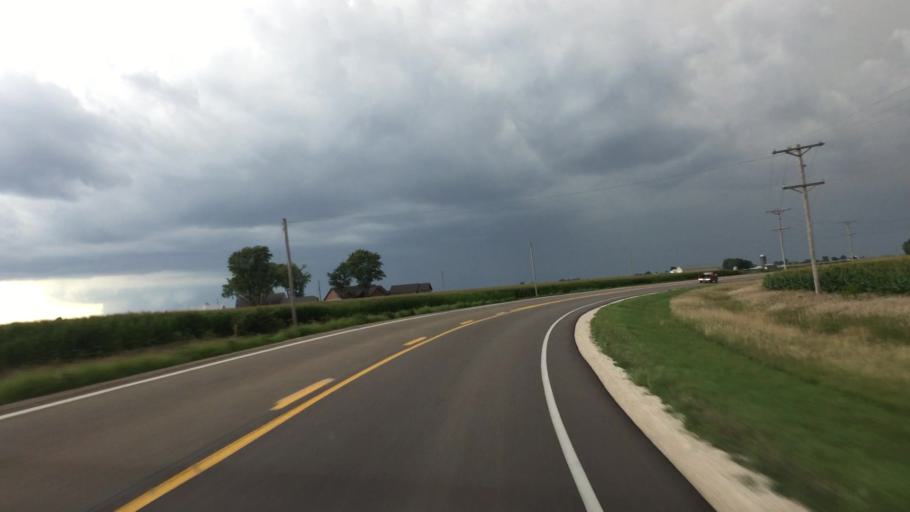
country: US
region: Iowa
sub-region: Henry County
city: New London
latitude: 40.7733
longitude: -91.4740
